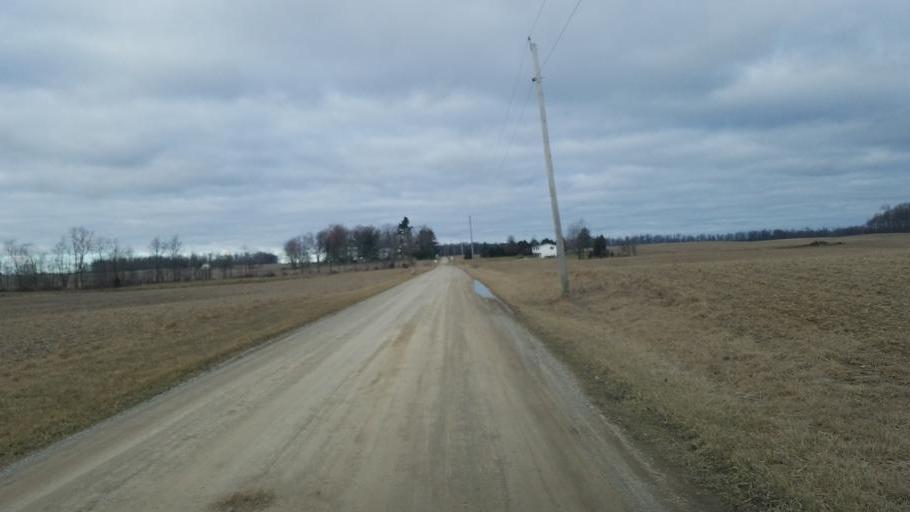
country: US
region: Ohio
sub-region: Richland County
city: Lexington
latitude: 40.5854
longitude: -82.6635
